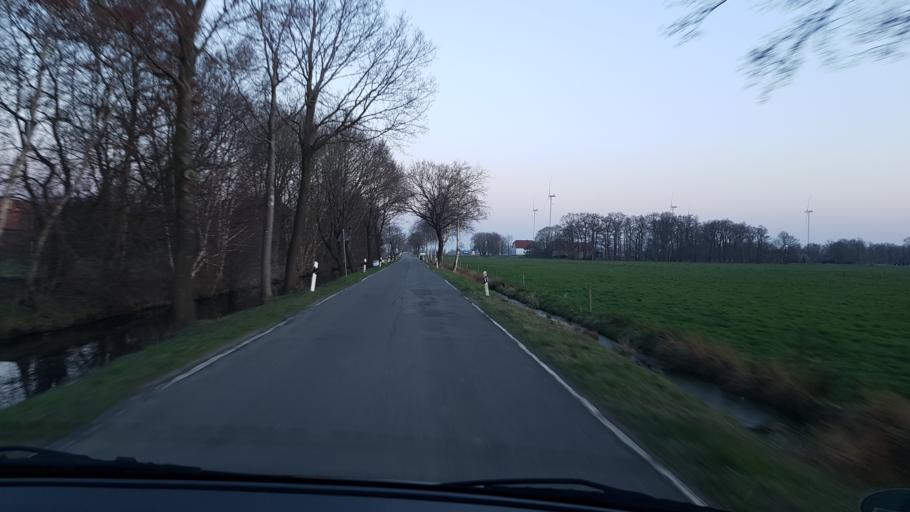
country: DE
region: Lower Saxony
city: Ovelgonne
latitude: 53.2867
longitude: 8.3642
